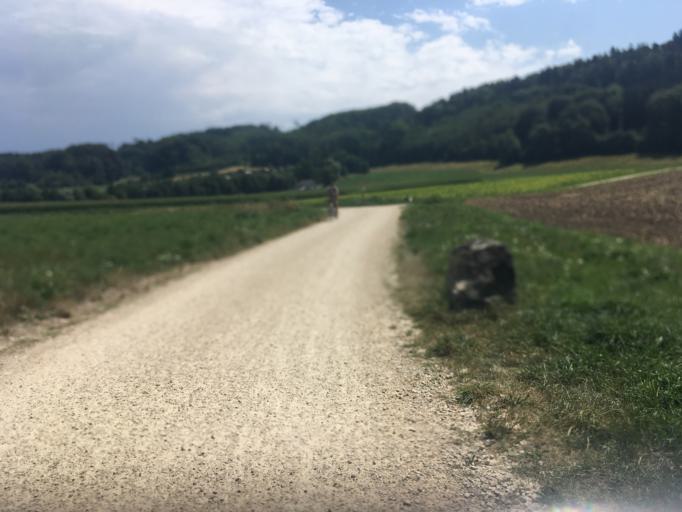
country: CH
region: Bern
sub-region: Biel/Bienne District
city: Brugg
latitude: 47.1155
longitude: 7.2682
